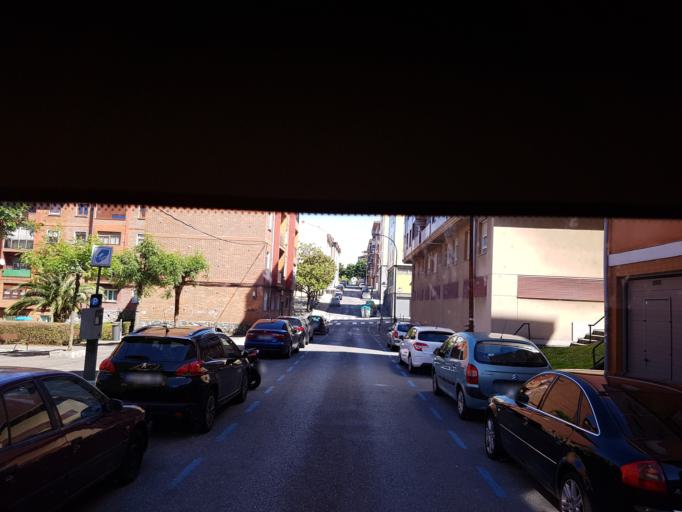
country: ES
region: Basque Country
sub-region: Bizkaia
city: Barakaldo
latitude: 43.2877
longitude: -2.9810
